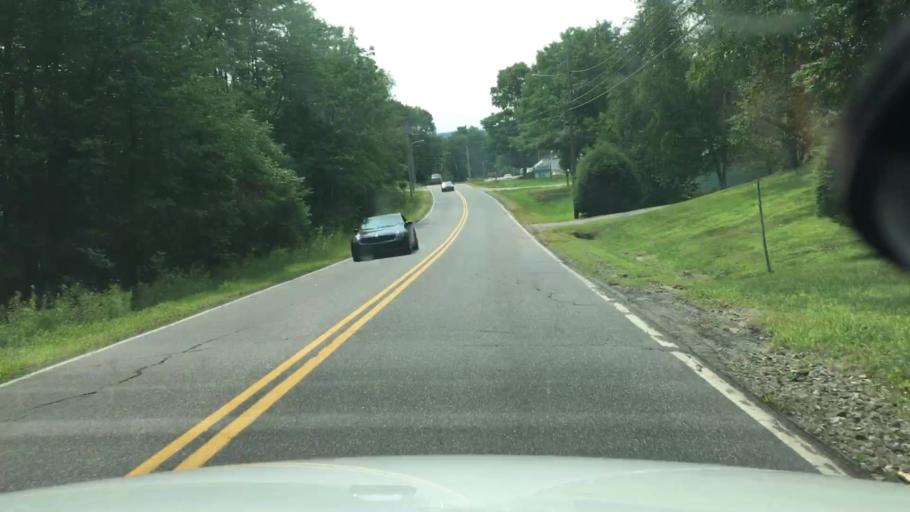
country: US
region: Maine
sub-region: Androscoggin County
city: Livermore Falls
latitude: 44.4836
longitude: -70.1863
